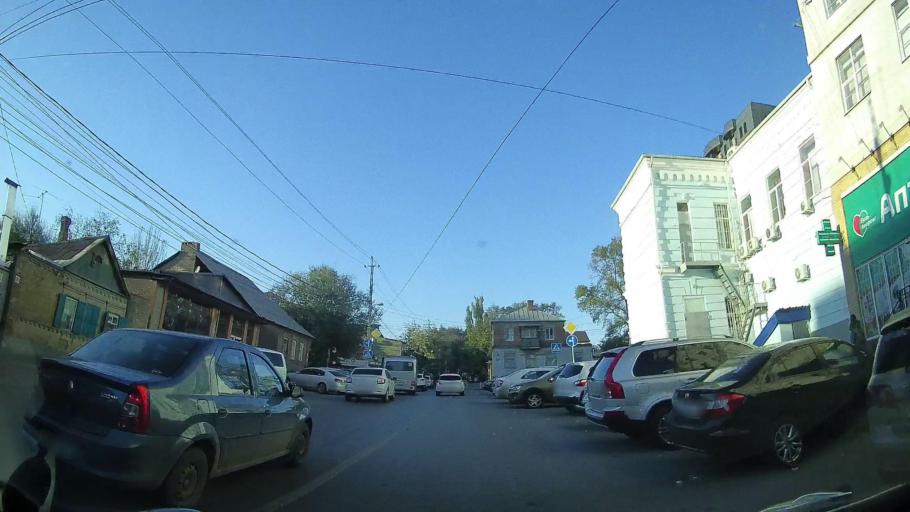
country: RU
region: Rostov
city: Rostov-na-Donu
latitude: 47.2280
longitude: 39.6945
